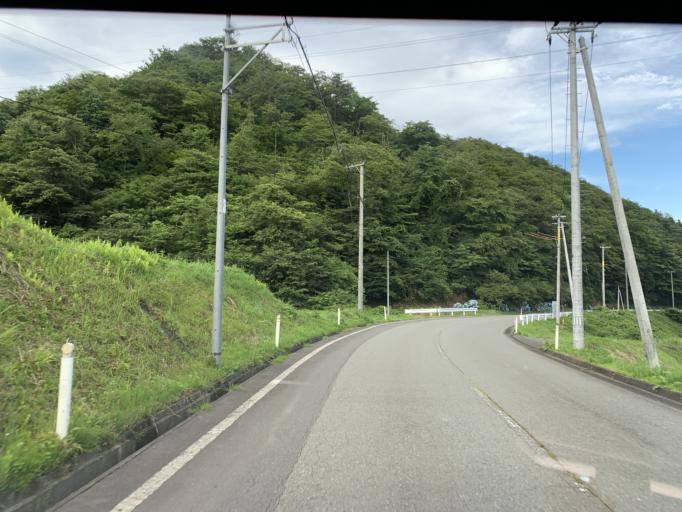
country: JP
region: Iwate
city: Ichinoseki
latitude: 38.9004
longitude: 140.9972
